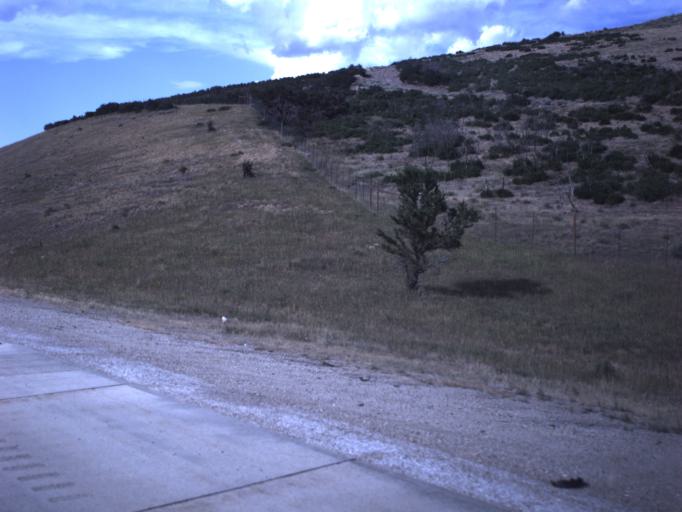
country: US
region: Utah
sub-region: Summit County
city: Park City
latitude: 40.6513
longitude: -111.4560
